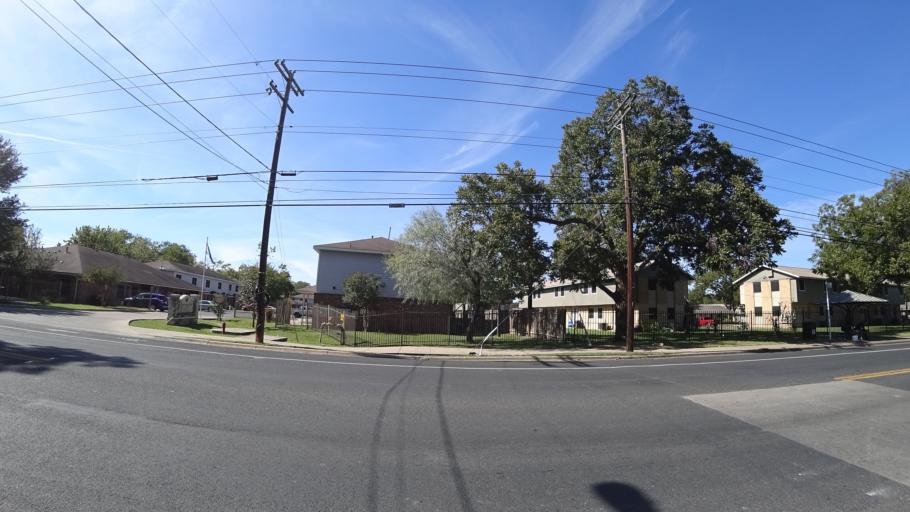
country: US
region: Texas
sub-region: Travis County
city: Austin
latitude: 30.2706
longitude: -97.6922
